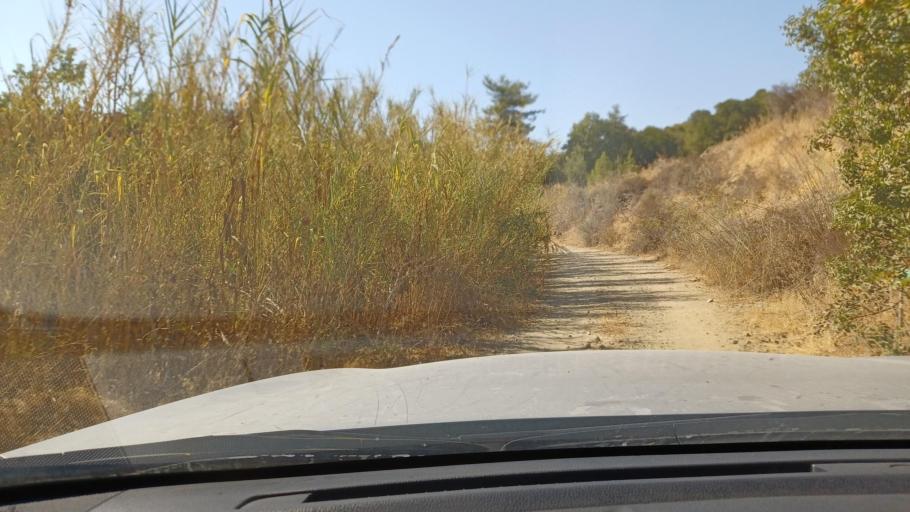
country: CY
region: Pafos
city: Polis
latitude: 35.0032
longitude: 32.4942
